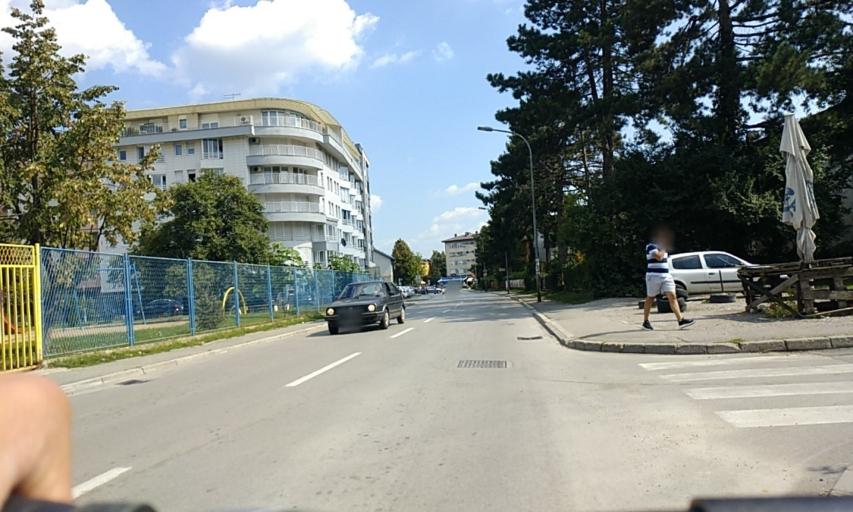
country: BA
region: Republika Srpska
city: Hiseti
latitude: 44.7653
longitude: 17.1821
